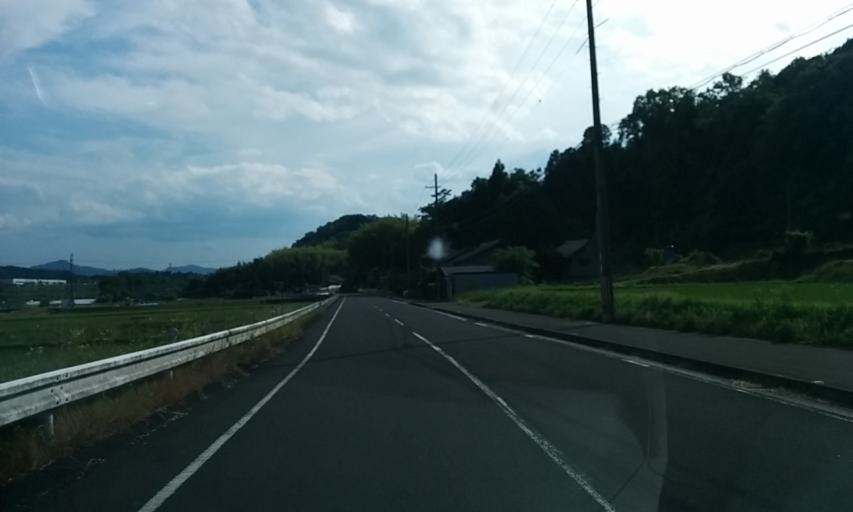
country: JP
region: Kyoto
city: Ayabe
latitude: 35.3381
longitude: 135.3042
